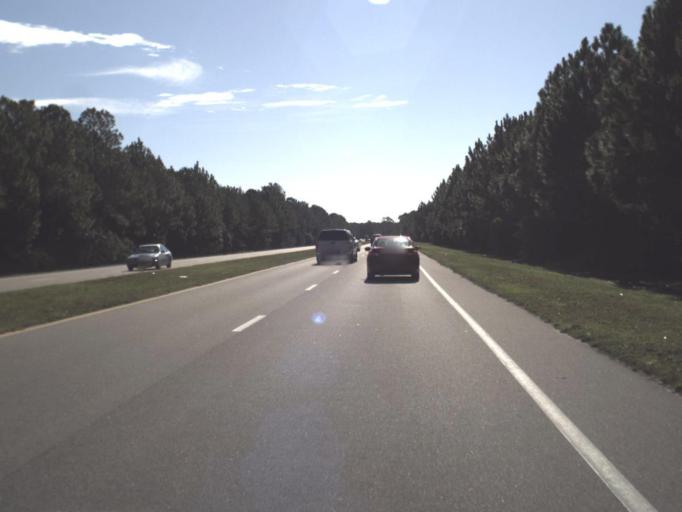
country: US
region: Florida
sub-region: Volusia County
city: Holly Hill
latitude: 29.2221
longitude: -81.0844
